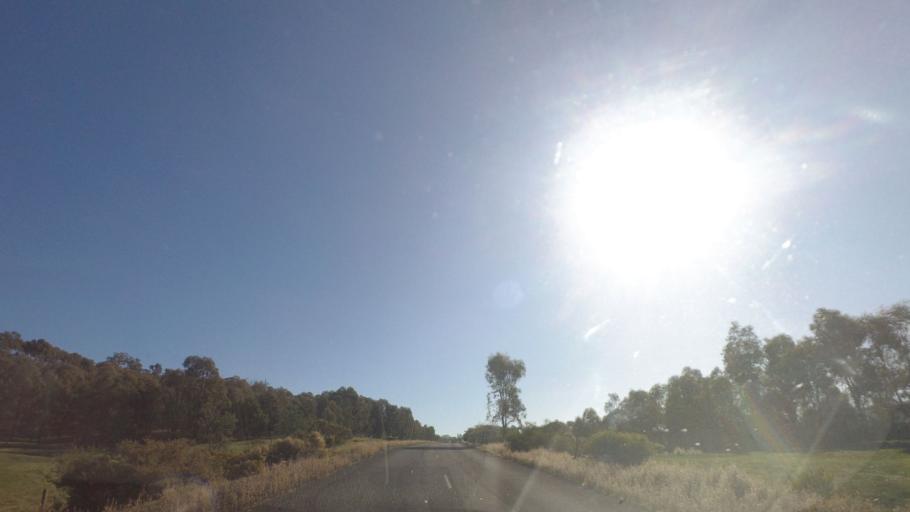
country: AU
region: Victoria
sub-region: Mount Alexander
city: Castlemaine
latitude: -37.0414
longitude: 144.2797
